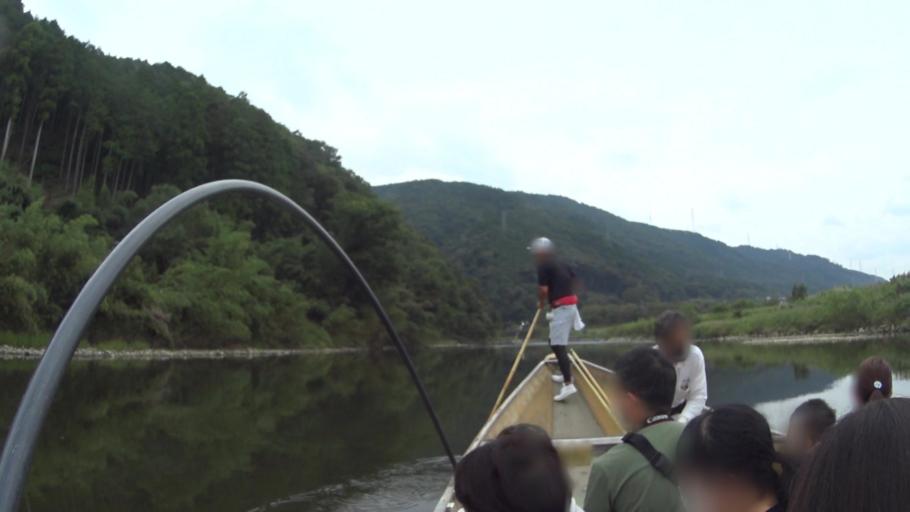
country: JP
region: Kyoto
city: Kameoka
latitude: 35.0155
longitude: 135.6042
